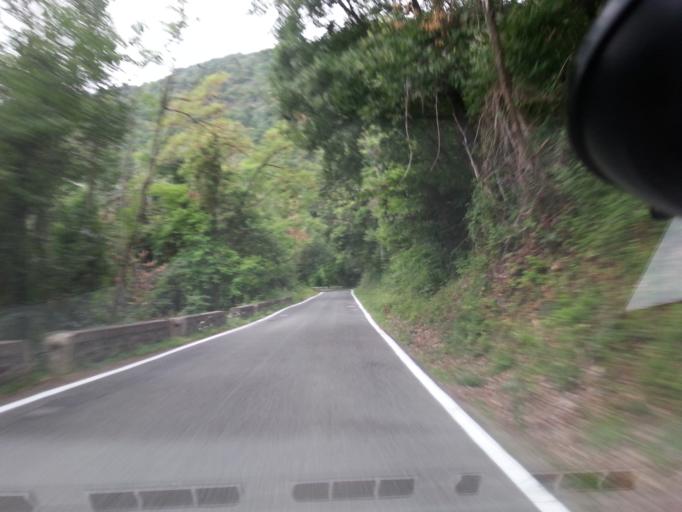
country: IT
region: Piedmont
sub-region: Provincia di Torino
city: Sant'Ambrogio di Torino
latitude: 45.0846
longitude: 7.3591
